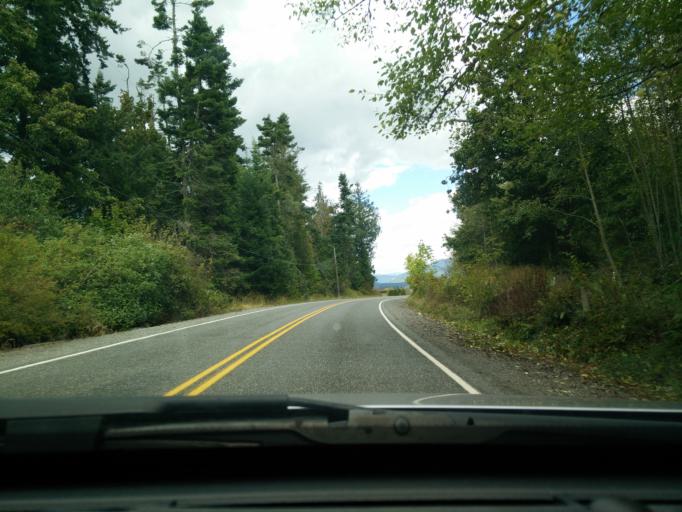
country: US
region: Washington
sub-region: Skagit County
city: Anacortes
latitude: 48.5143
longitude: -122.4810
